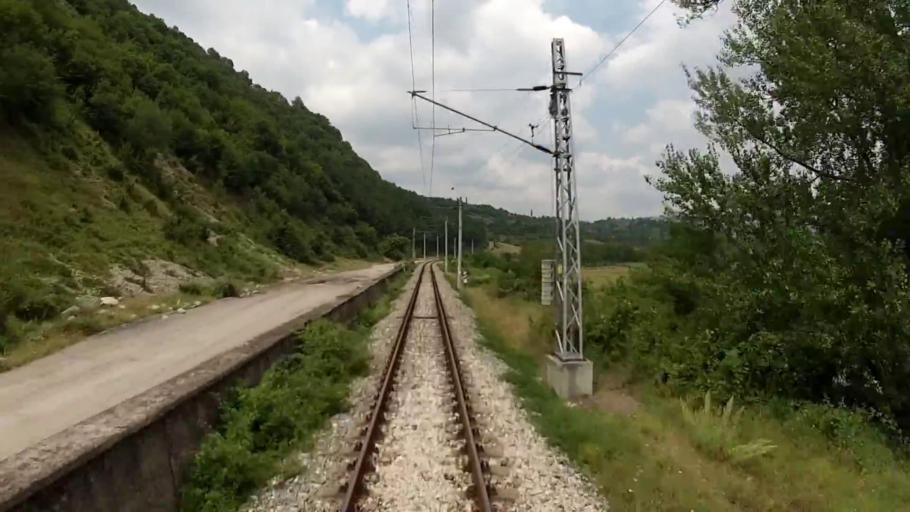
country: BG
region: Blagoevgrad
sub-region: Obshtina Simitli
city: Simitli
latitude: 41.8441
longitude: 23.1486
